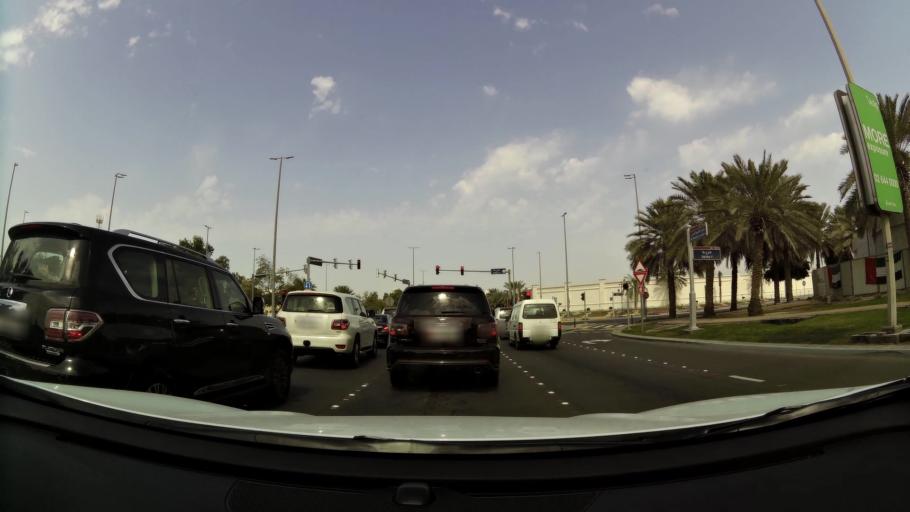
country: AE
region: Abu Dhabi
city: Abu Dhabi
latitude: 24.4500
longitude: 54.3619
